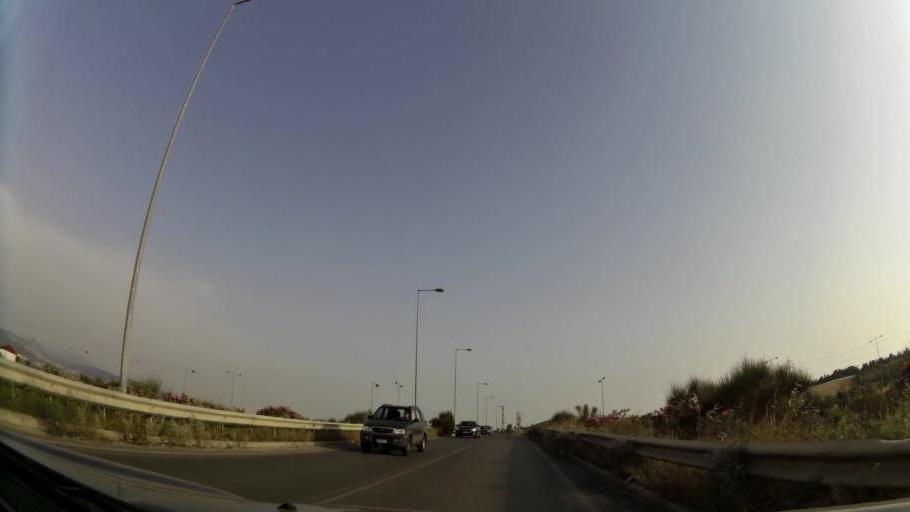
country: GR
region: Central Macedonia
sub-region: Nomos Thessalonikis
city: Evosmos
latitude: 40.6964
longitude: 22.9096
